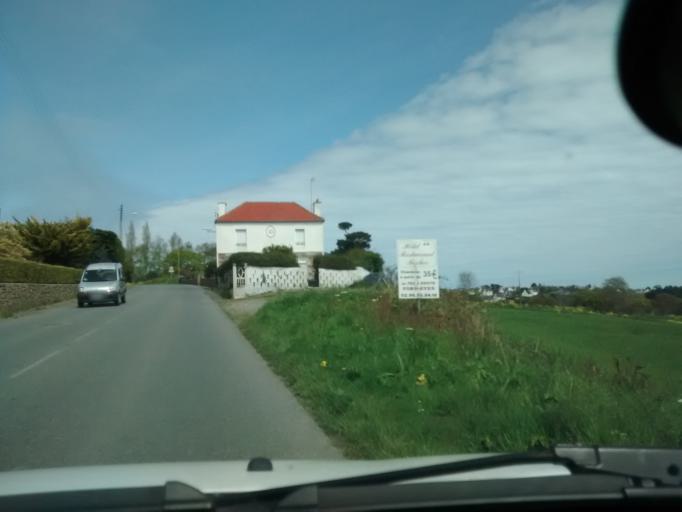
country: FR
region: Brittany
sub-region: Departement des Cotes-d'Armor
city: Ploubazlanec
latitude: 48.7932
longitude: -3.0354
